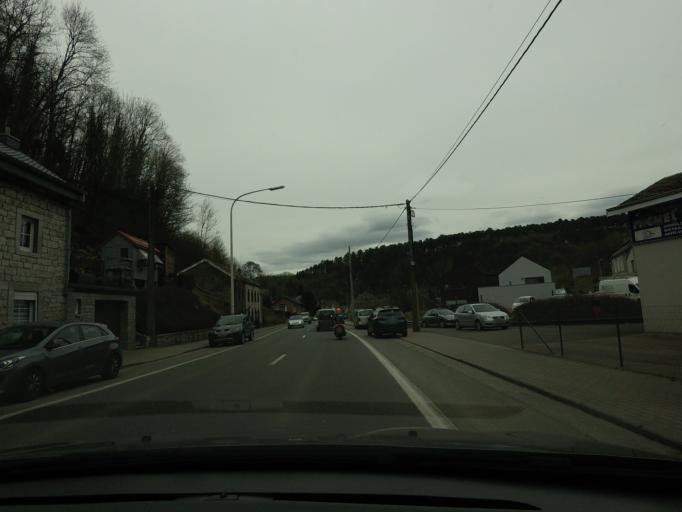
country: BE
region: Wallonia
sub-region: Province de Liege
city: Aywaille
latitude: 50.4674
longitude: 5.6788
